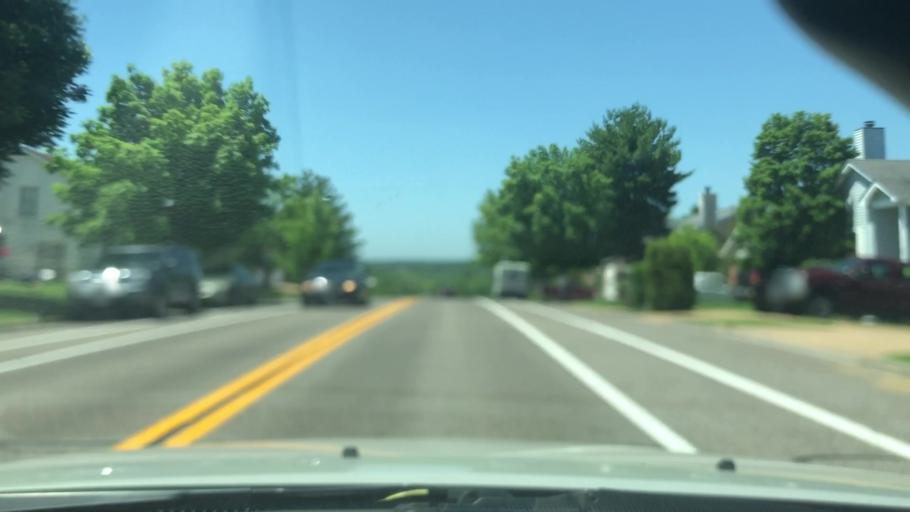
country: US
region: Missouri
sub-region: Jefferson County
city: Arnold
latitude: 38.4704
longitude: -90.3516
